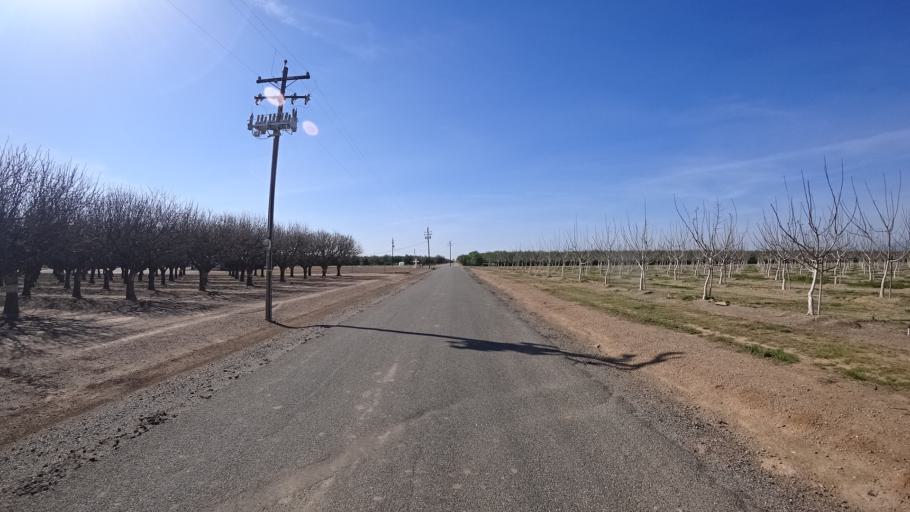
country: US
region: California
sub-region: Glenn County
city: Willows
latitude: 39.6126
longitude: -122.2129
